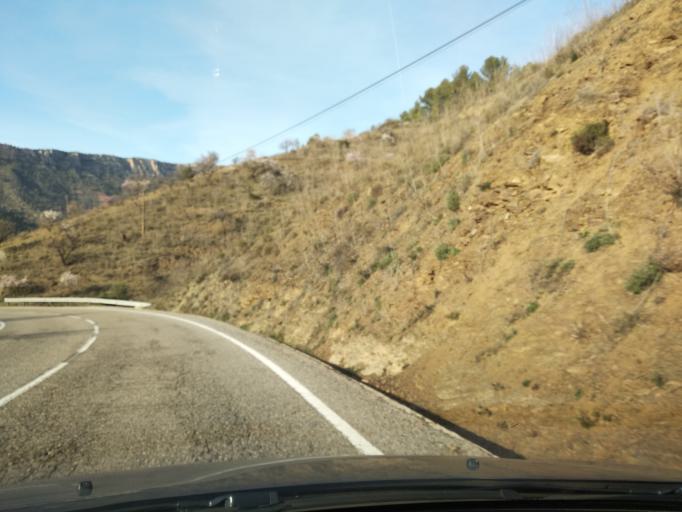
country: ES
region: Catalonia
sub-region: Provincia de Tarragona
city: Margalef
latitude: 41.2136
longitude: 0.7694
